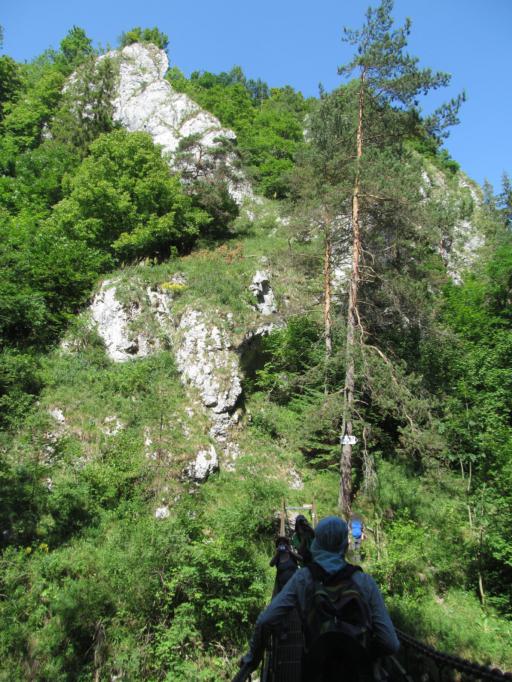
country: SK
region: Kosicky
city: Spisska Nova Ves
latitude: 48.9543
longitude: 20.4367
